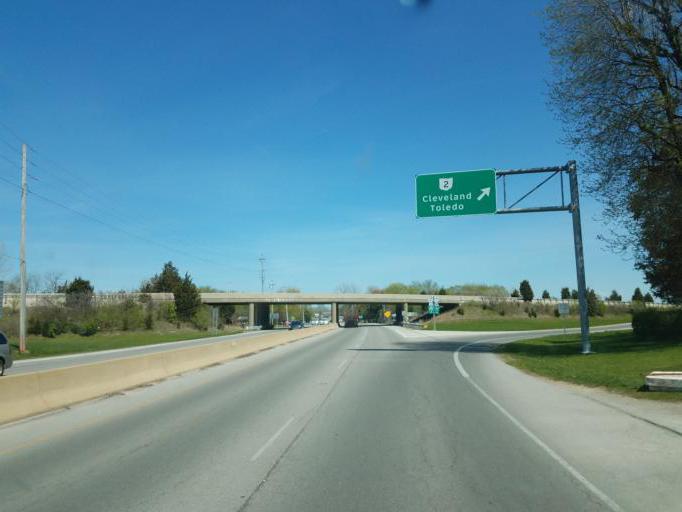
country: US
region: Ohio
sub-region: Ottawa County
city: Port Clinton
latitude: 41.5150
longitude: -82.9098
